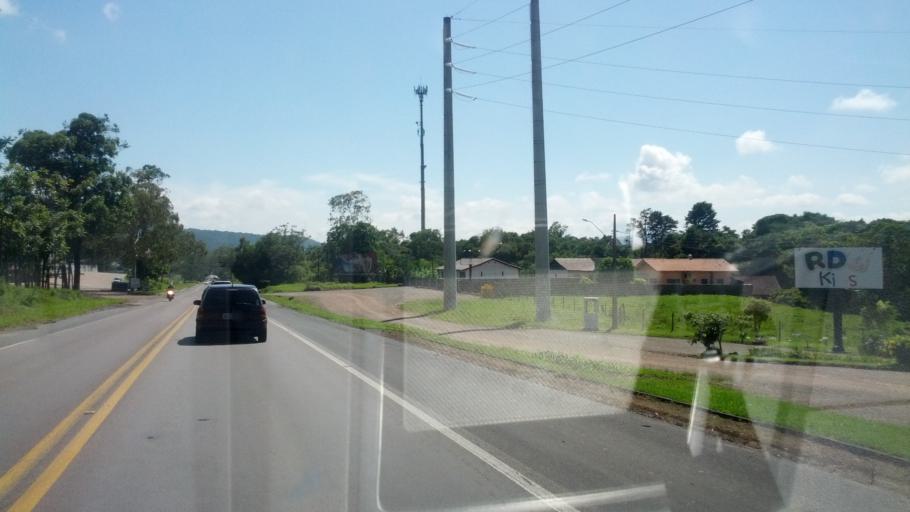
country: BR
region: Santa Catarina
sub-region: Rio Do Sul
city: Rio do Sul
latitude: -27.1841
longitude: -49.6035
